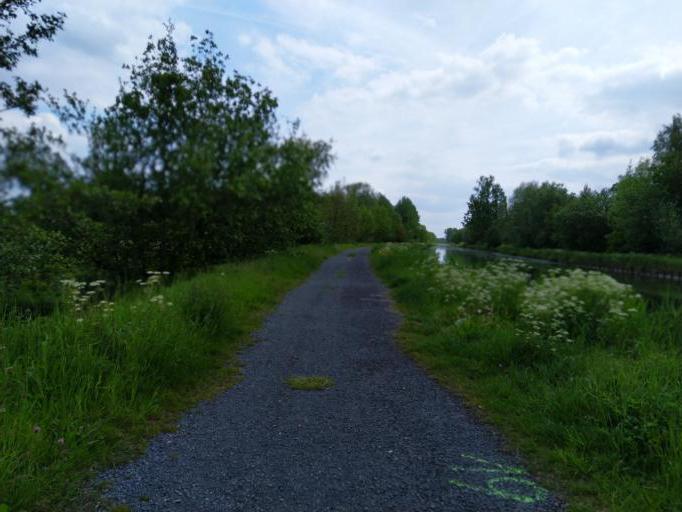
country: FR
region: Nord-Pas-de-Calais
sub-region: Departement du Nord
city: Landrecies
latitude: 50.0749
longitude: 3.6473
